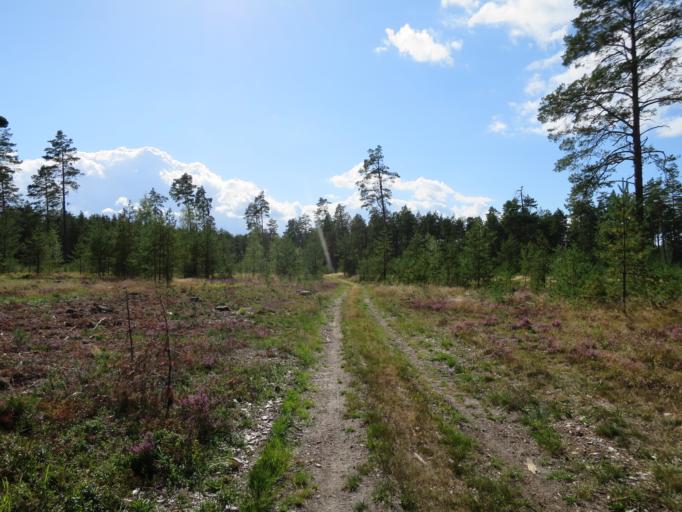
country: LV
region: Riga
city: Jaunciems
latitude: 57.0594
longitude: 24.2249
